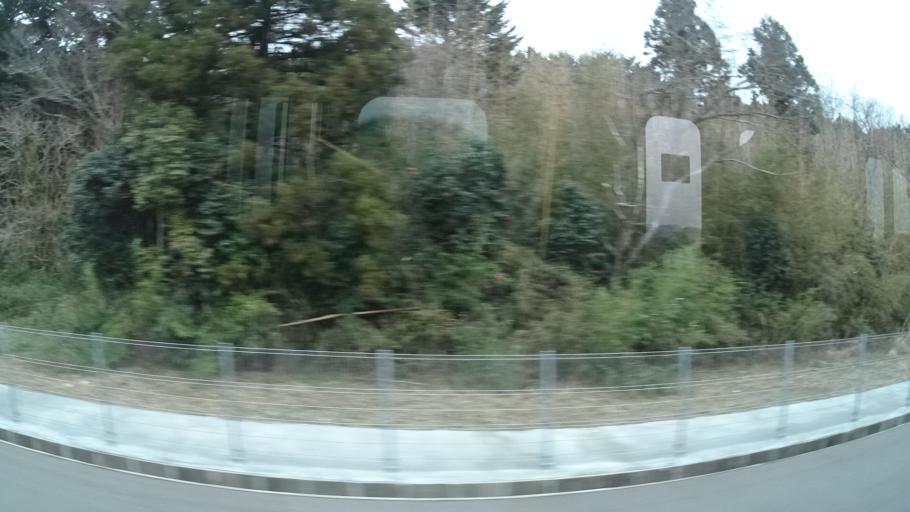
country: JP
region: Fukushima
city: Namie
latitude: 37.4336
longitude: 141.0010
